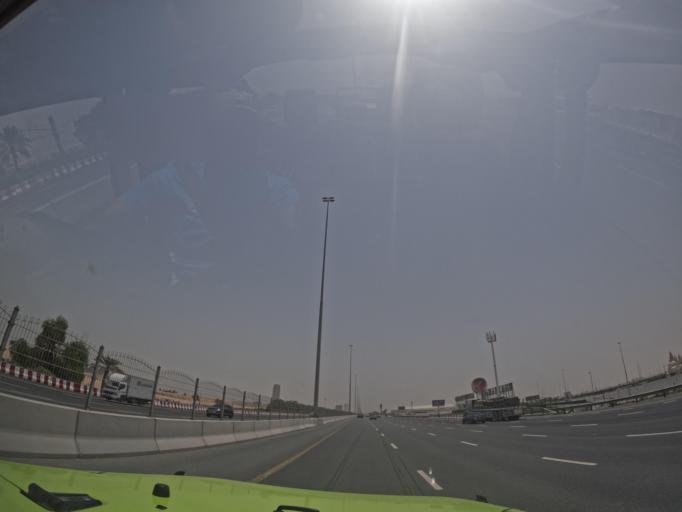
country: AE
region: Dubai
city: Dubai
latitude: 25.0730
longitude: 55.3025
